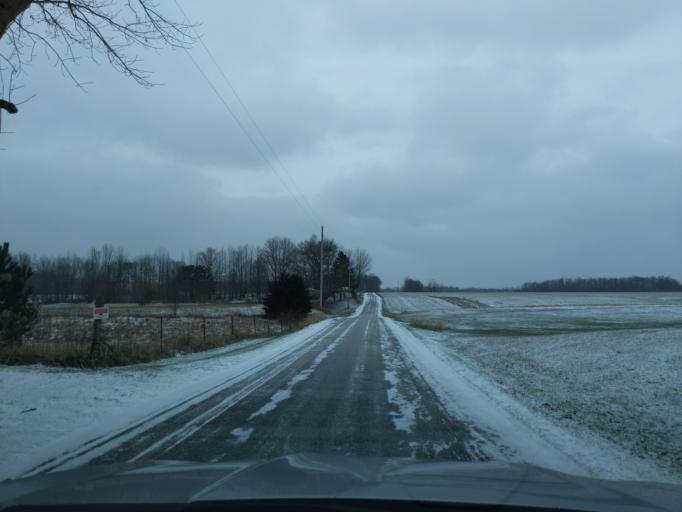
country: US
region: Indiana
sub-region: Decatur County
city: Greensburg
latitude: 39.2483
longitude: -85.4532
